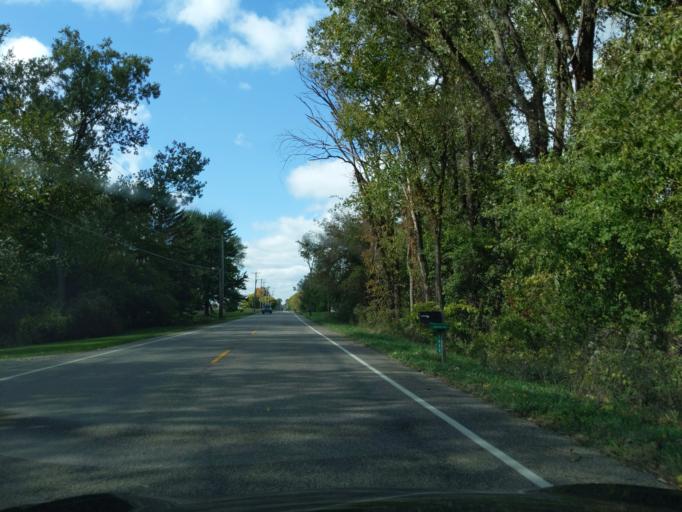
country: US
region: Michigan
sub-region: Eaton County
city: Charlotte
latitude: 42.5675
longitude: -84.7981
